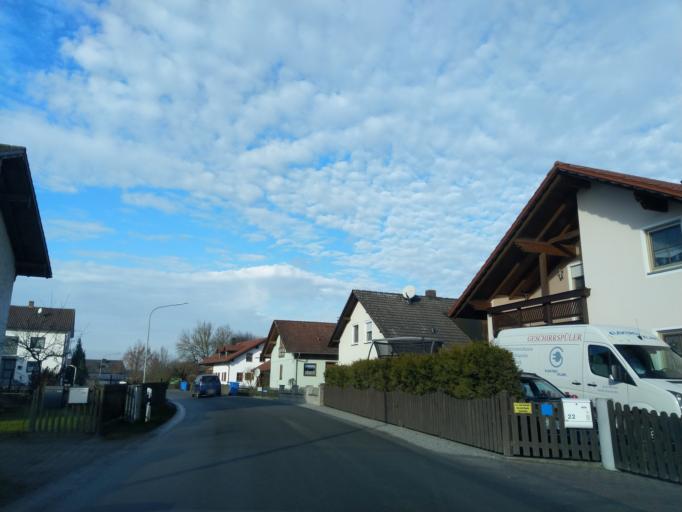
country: DE
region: Bavaria
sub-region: Lower Bavaria
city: Osterhofen
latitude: 48.7226
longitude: 13.0120
